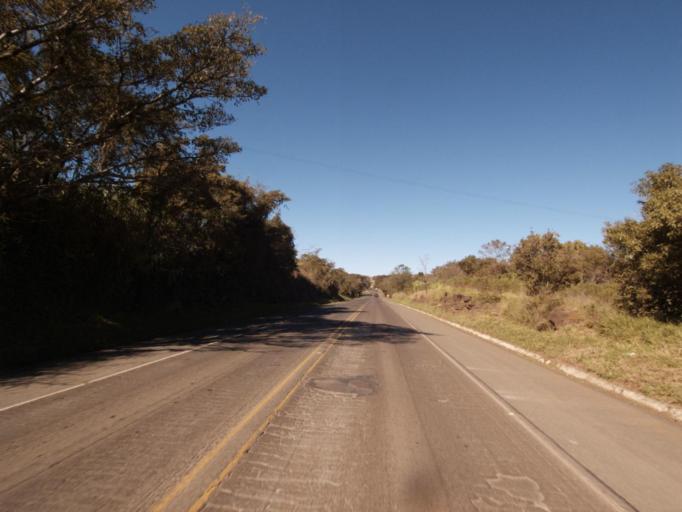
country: BR
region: Santa Catarina
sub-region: Chapeco
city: Chapeco
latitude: -26.9692
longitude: -52.7526
